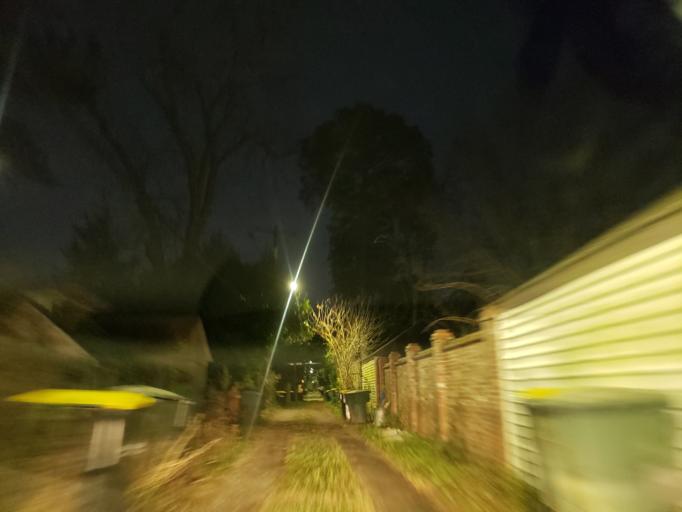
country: US
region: Georgia
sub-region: Chatham County
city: Savannah
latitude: 32.0442
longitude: -81.0968
